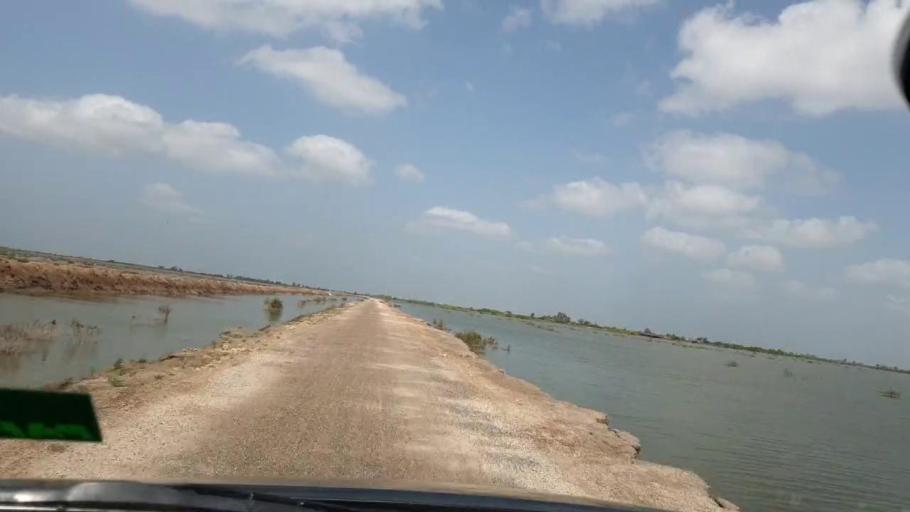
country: PK
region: Sindh
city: Kadhan
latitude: 24.5888
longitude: 69.1375
